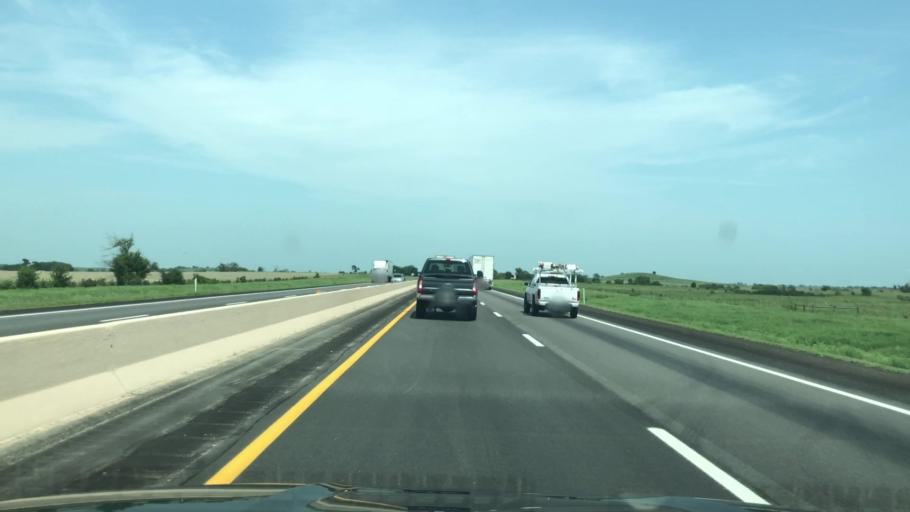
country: US
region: Oklahoma
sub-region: Ottawa County
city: Afton
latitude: 36.6796
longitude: -95.0454
